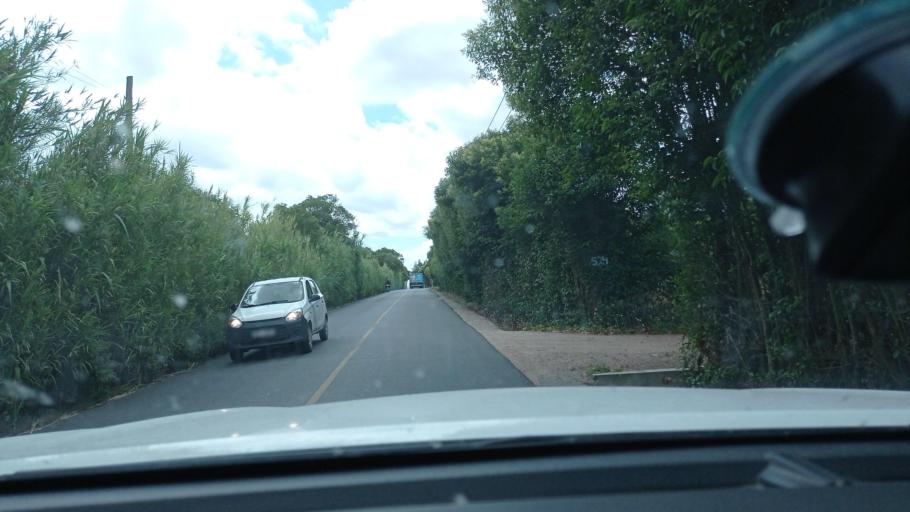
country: UY
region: Canelones
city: La Paz
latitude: -34.8059
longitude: -56.2049
